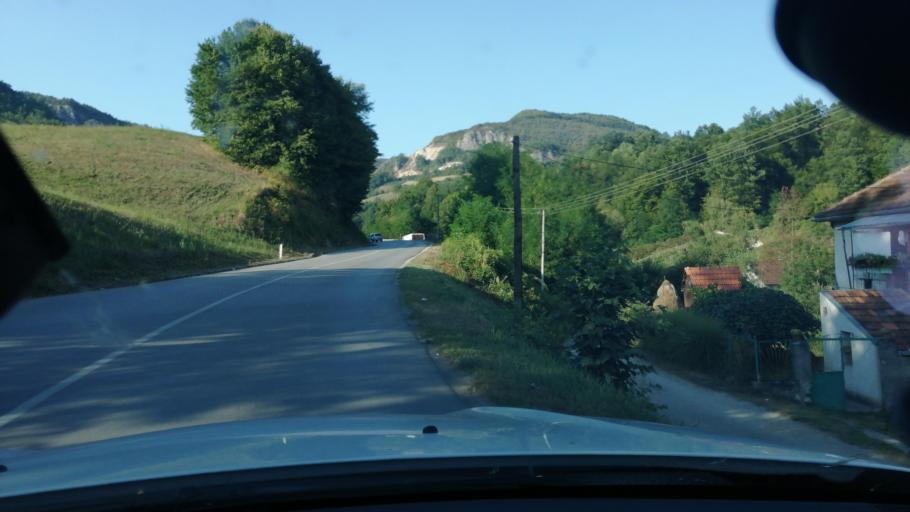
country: RS
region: Central Serbia
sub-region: Moravicki Okrug
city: Ivanjica
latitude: 43.6136
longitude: 20.2369
